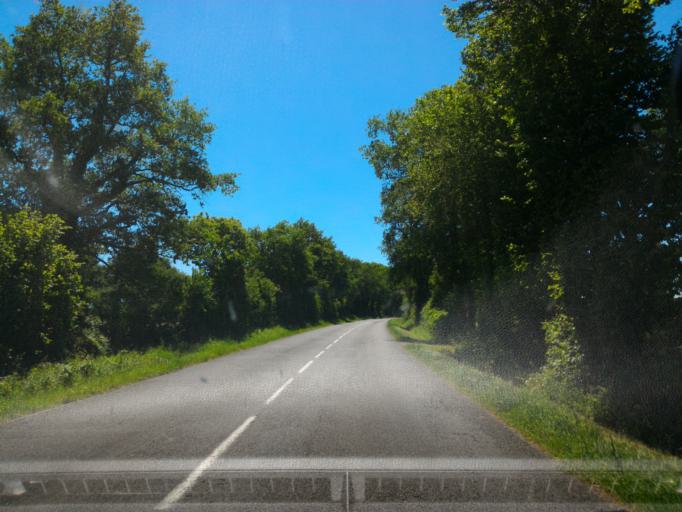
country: FR
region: Poitou-Charentes
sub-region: Departement de la Vienne
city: Availles-Limouzine
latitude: 46.1669
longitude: 0.7282
